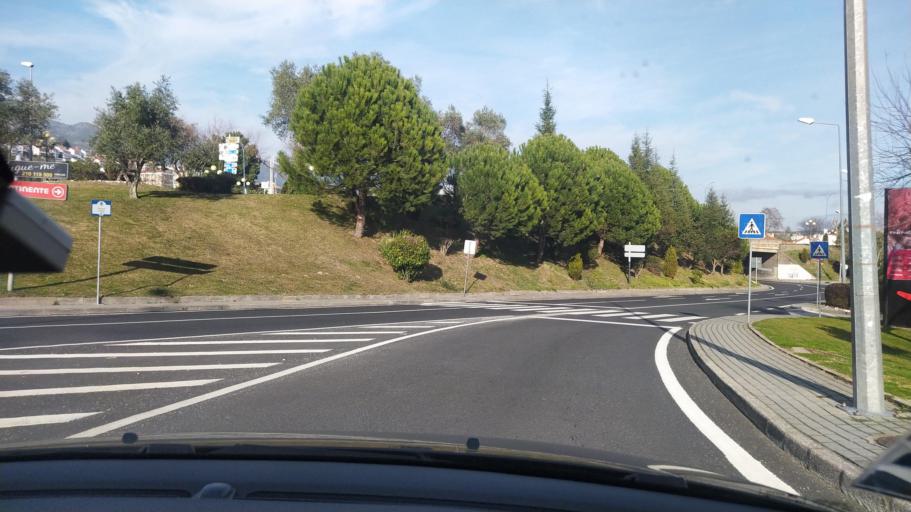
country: PT
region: Castelo Branco
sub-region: Covilha
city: Covilha
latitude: 40.2652
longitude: -7.5035
